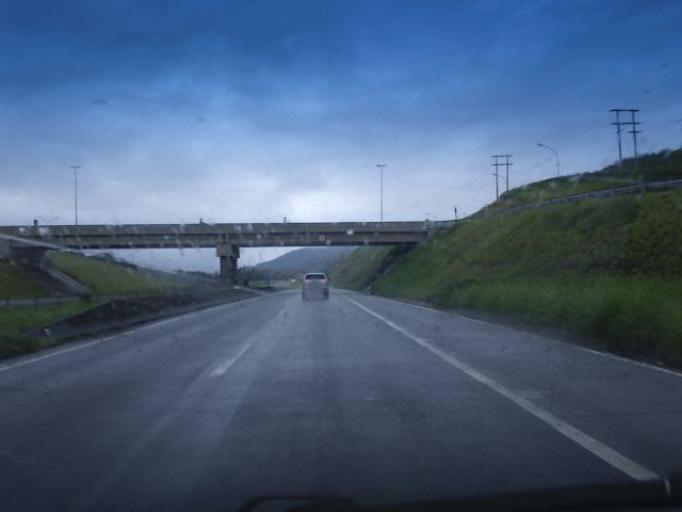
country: BR
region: Sao Paulo
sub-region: Juquia
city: Juquia
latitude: -24.3286
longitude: -47.5749
